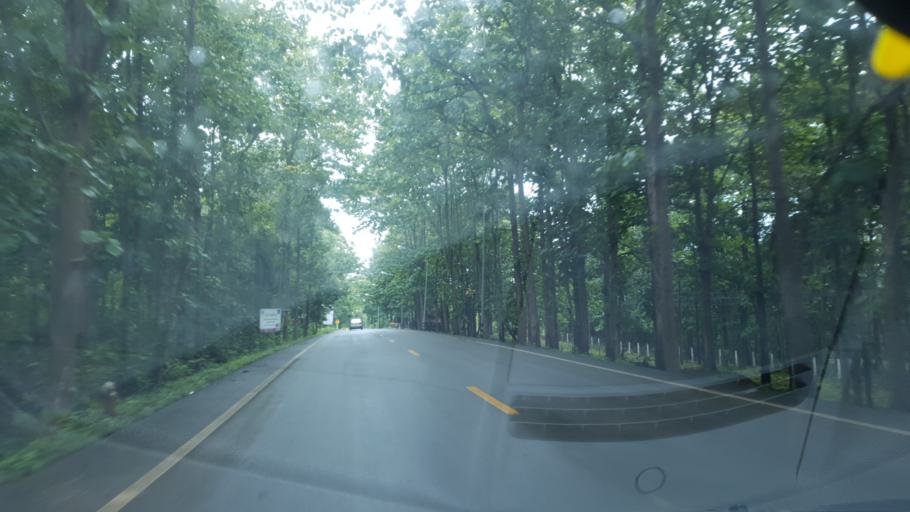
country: TH
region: Mae Hong Son
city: Pa Pae
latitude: 18.2089
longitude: 97.9379
